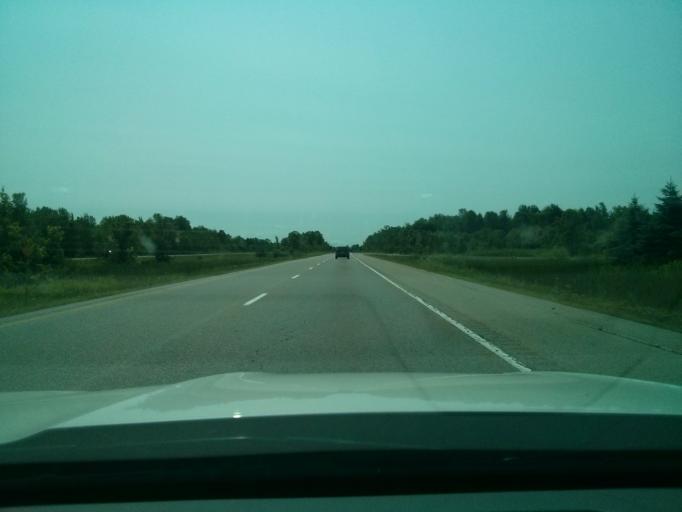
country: CA
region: Ontario
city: Prescott
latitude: 44.8446
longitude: -75.5352
